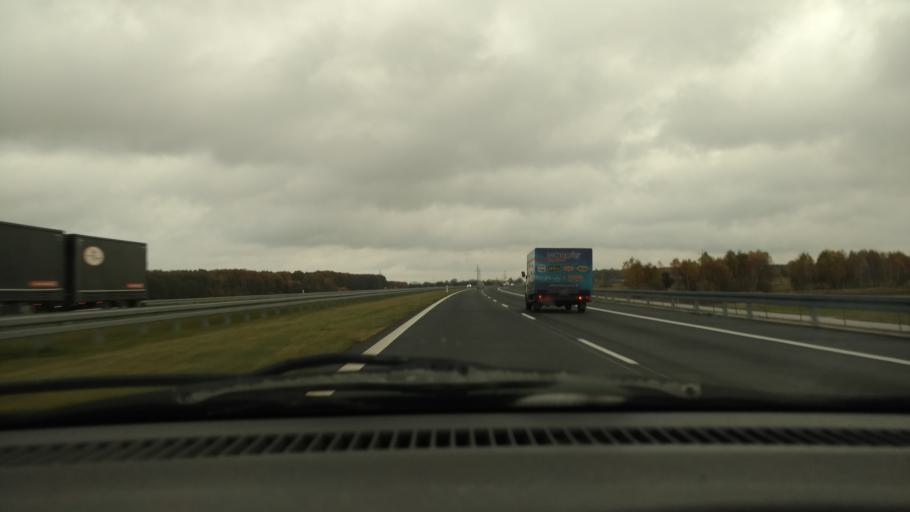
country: PL
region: Lodz Voivodeship
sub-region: Powiat pabianicki
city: Dobron
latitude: 51.6063
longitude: 19.3026
